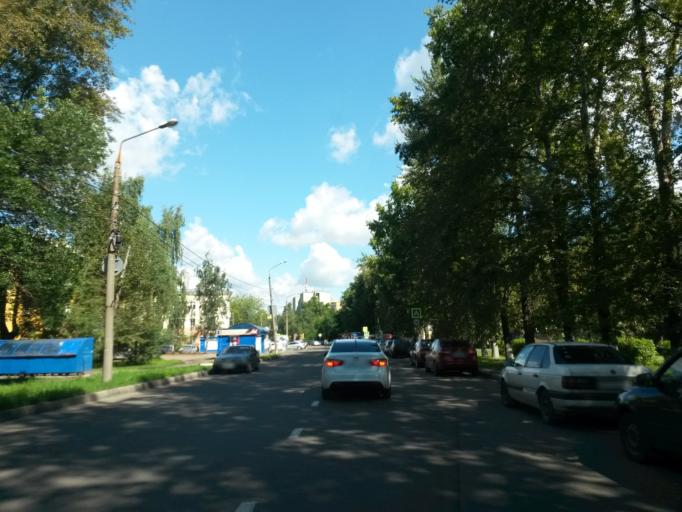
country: RU
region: Jaroslavl
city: Yaroslavl
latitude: 57.5952
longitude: 39.8786
